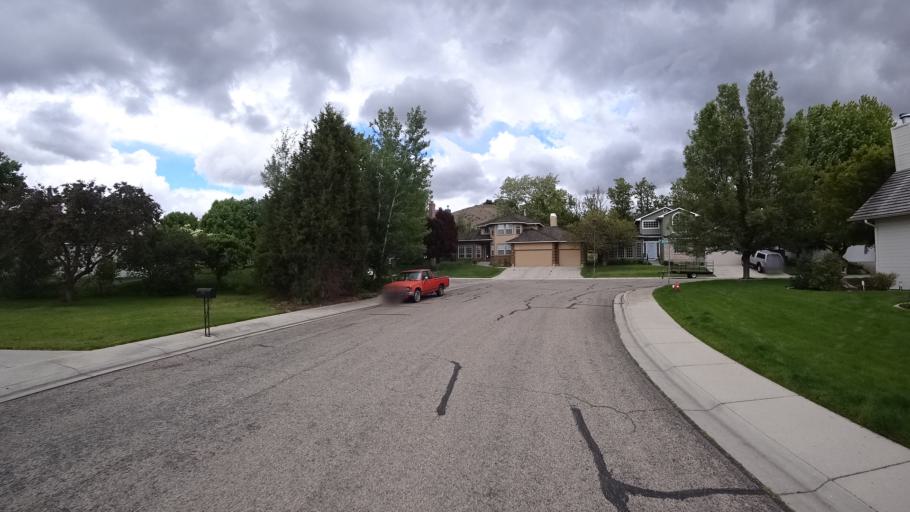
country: US
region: Idaho
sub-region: Ada County
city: Garden City
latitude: 43.6723
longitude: -116.2623
